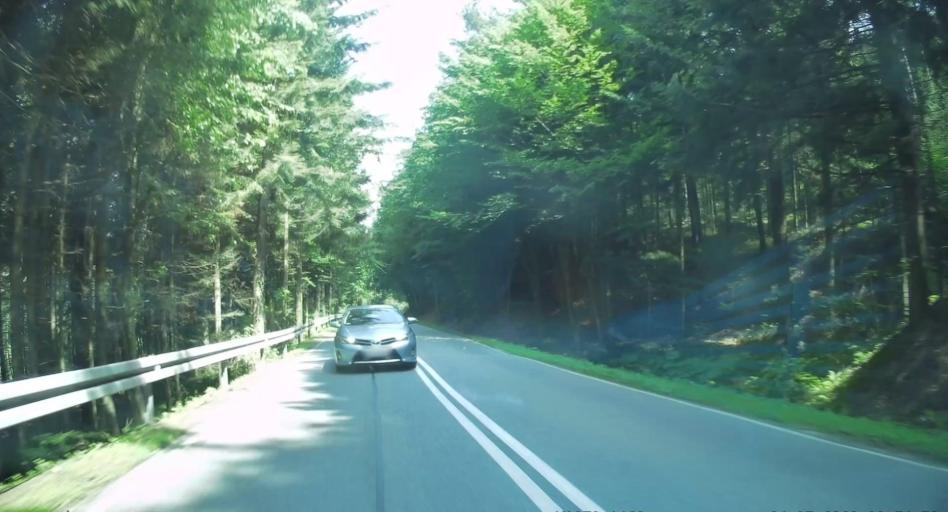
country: PL
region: Lesser Poland Voivodeship
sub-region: Powiat tarnowski
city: Zakliczyn
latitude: 49.7722
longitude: 20.7744
